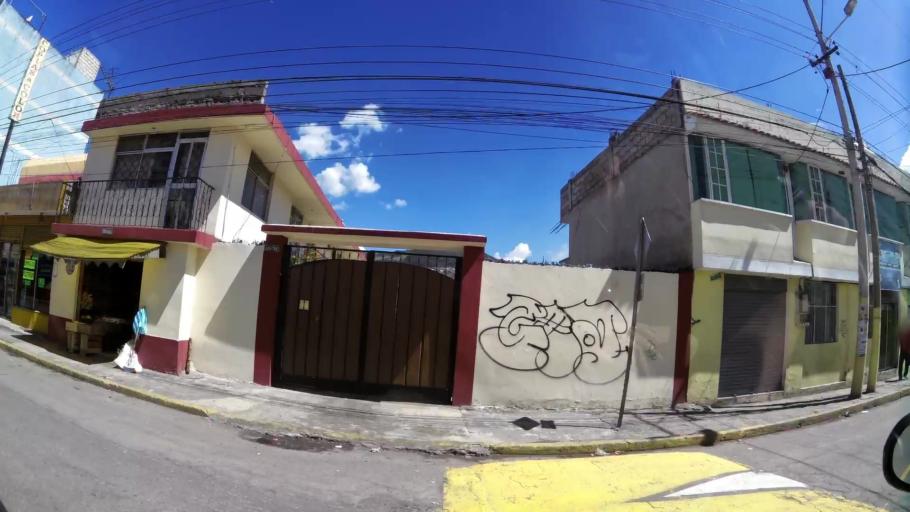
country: EC
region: Pichincha
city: Quito
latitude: -0.2696
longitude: -78.5474
